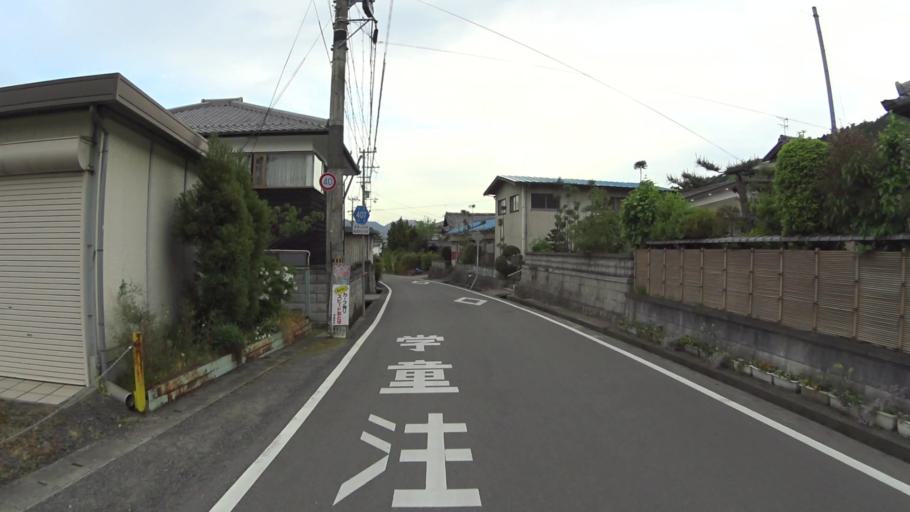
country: JP
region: Kyoto
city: Kameoka
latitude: 35.0311
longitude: 135.5424
